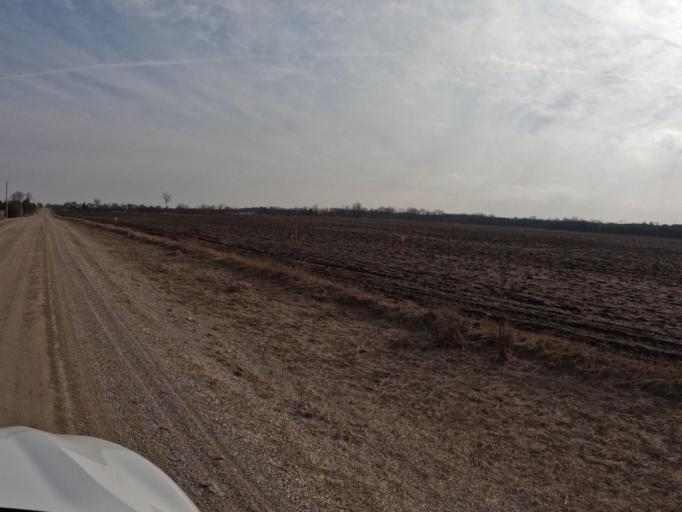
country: CA
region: Ontario
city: Orangeville
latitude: 43.9098
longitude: -80.2700
